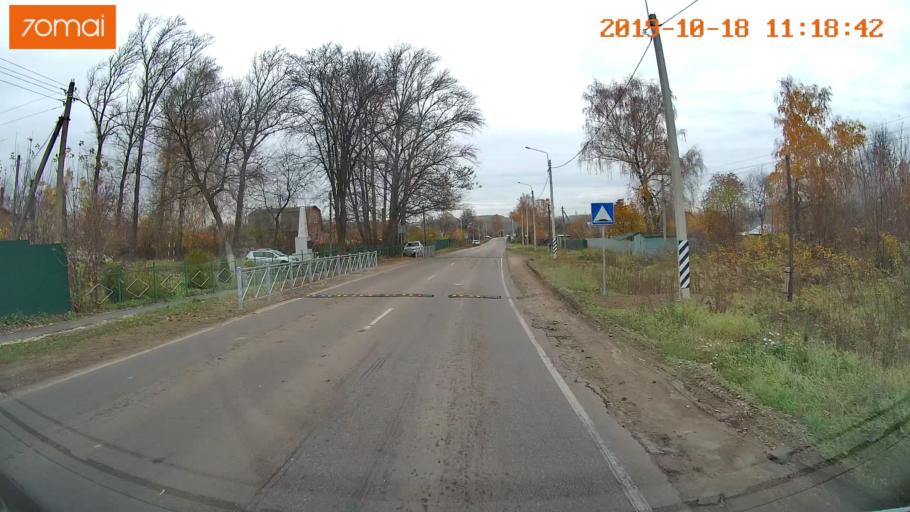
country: RU
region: Tula
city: Kimovsk
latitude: 54.0411
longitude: 38.5509
